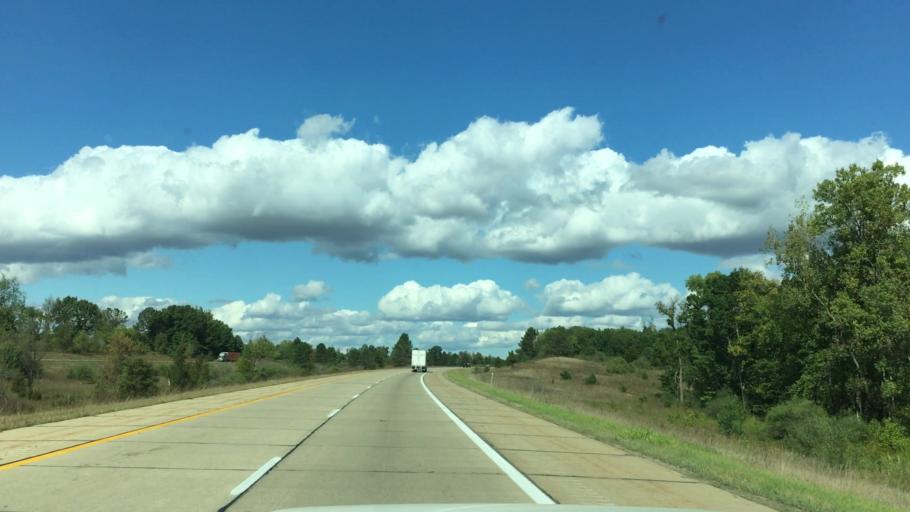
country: US
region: Michigan
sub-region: Eaton County
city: Olivet
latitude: 42.4055
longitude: -84.9684
